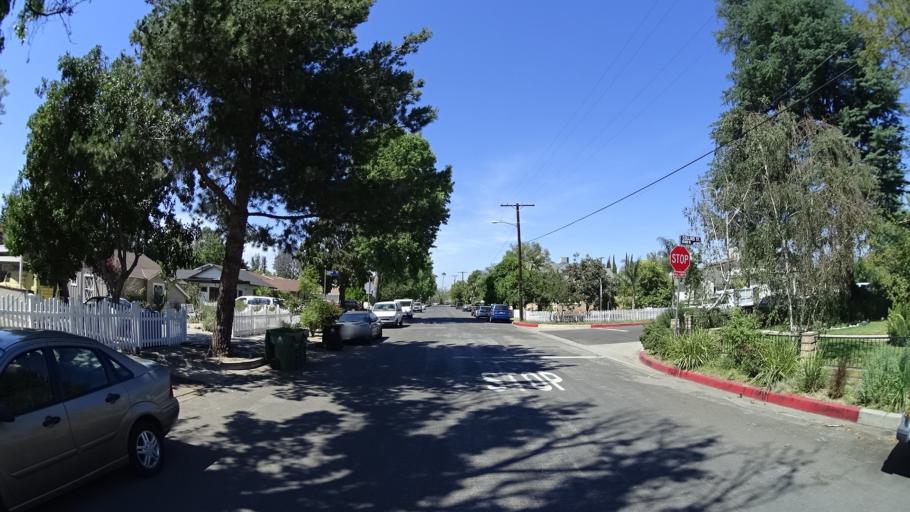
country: US
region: California
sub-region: Los Angeles County
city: North Hollywood
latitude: 34.1732
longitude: -118.4020
